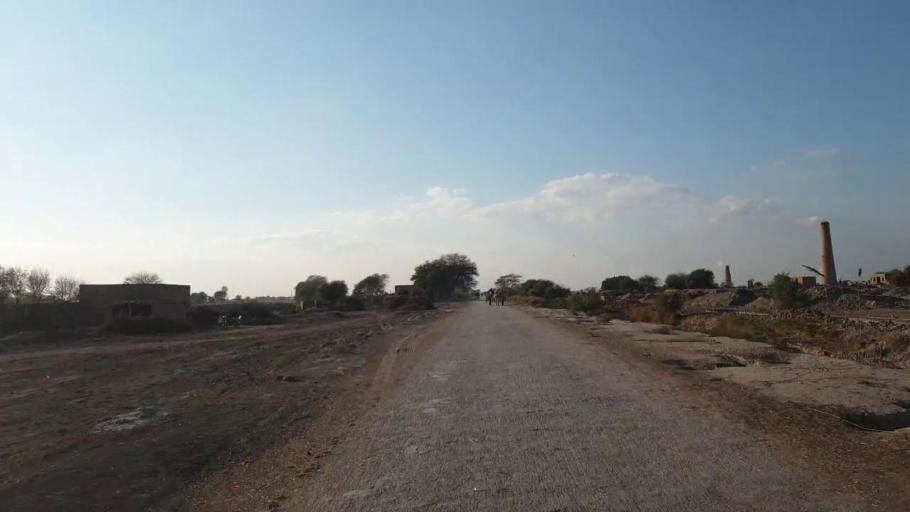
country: PK
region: Sindh
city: Shahpur Chakar
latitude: 26.1422
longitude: 68.5452
